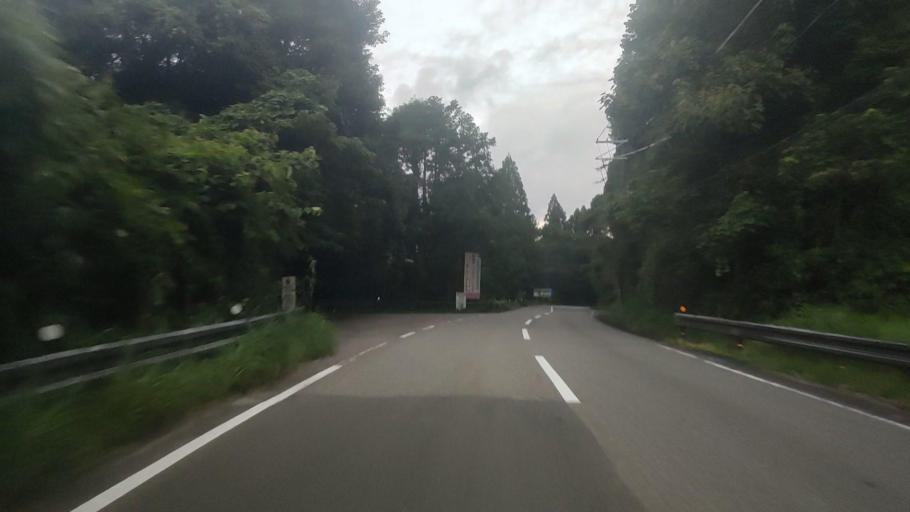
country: JP
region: Wakayama
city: Shingu
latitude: 33.7518
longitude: 135.9375
